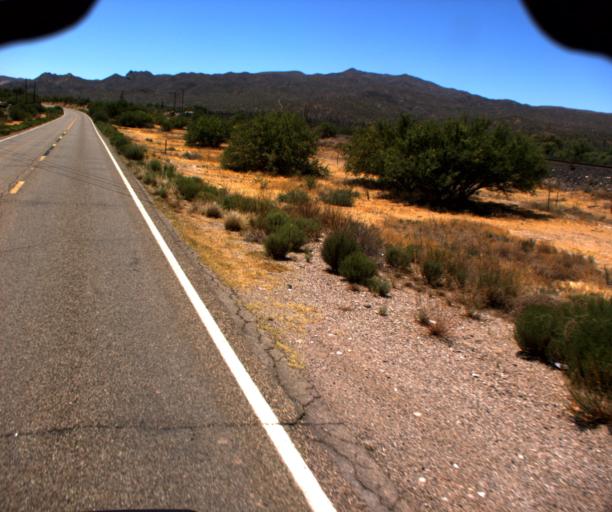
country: US
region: Arizona
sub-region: Pinal County
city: Kearny
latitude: 33.0370
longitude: -110.8810
